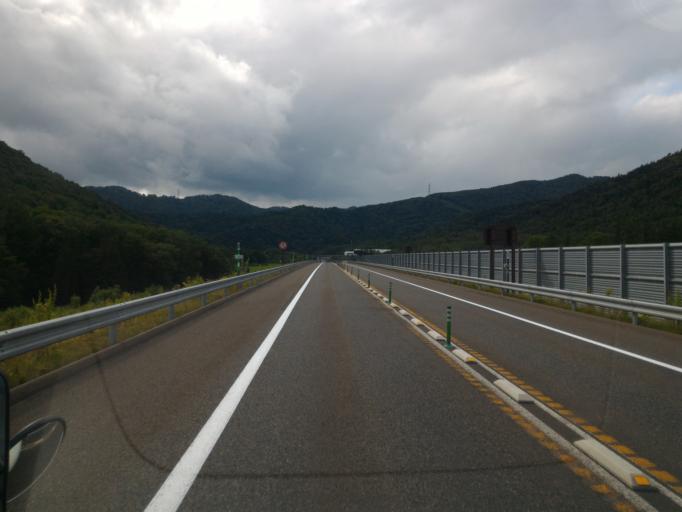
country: JP
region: Hokkaido
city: Shimo-furano
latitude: 43.0626
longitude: 142.5495
